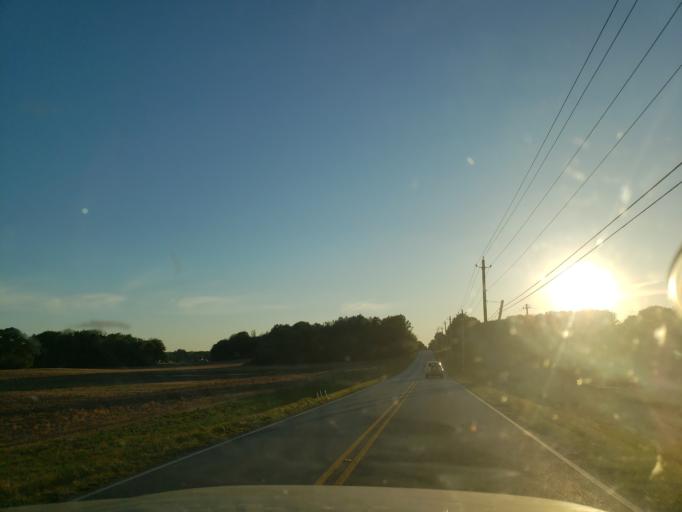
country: US
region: Alabama
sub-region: Madison County
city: Hazel Green
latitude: 34.9322
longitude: -86.5463
